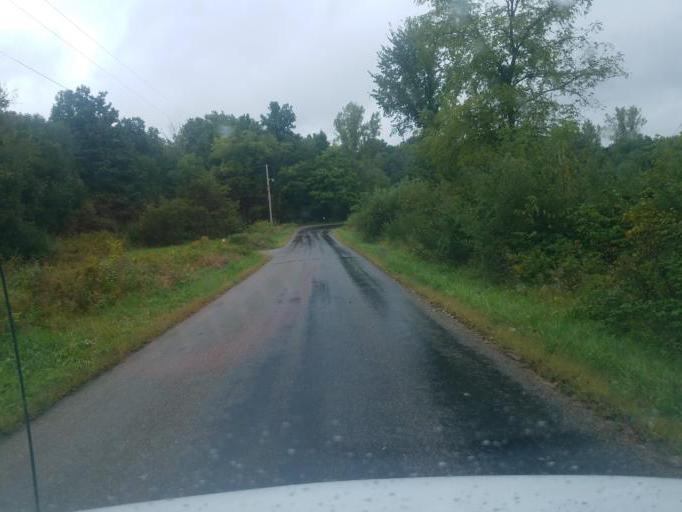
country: US
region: Ohio
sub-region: Wayne County
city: West Salem
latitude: 40.9308
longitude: -82.1260
